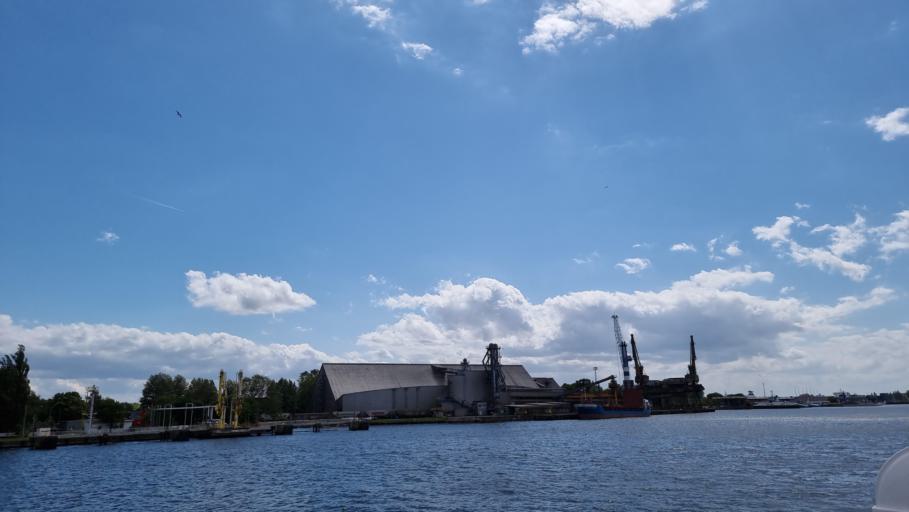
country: PL
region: West Pomeranian Voivodeship
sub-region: Swinoujscie
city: Swinoujscie
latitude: 53.9107
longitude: 14.2732
